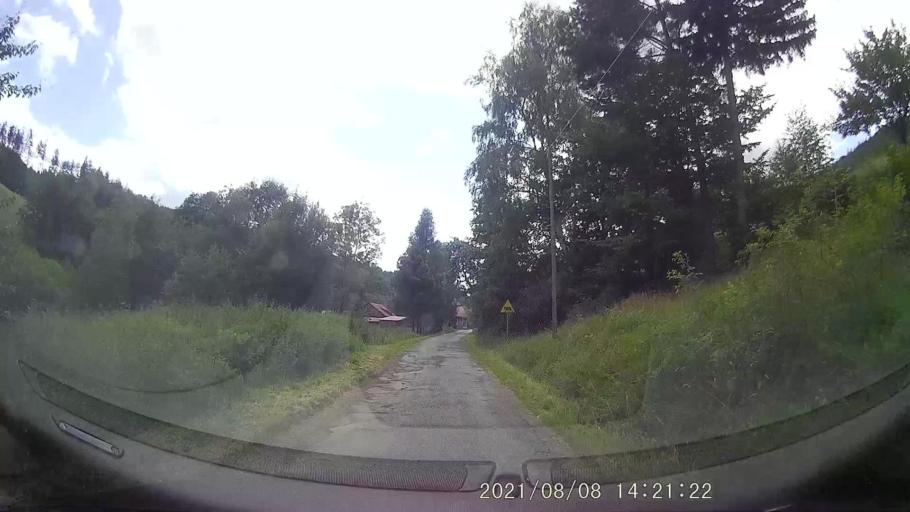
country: PL
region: Lower Silesian Voivodeship
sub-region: Powiat klodzki
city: Lewin Klodzki
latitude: 50.4443
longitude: 16.3110
